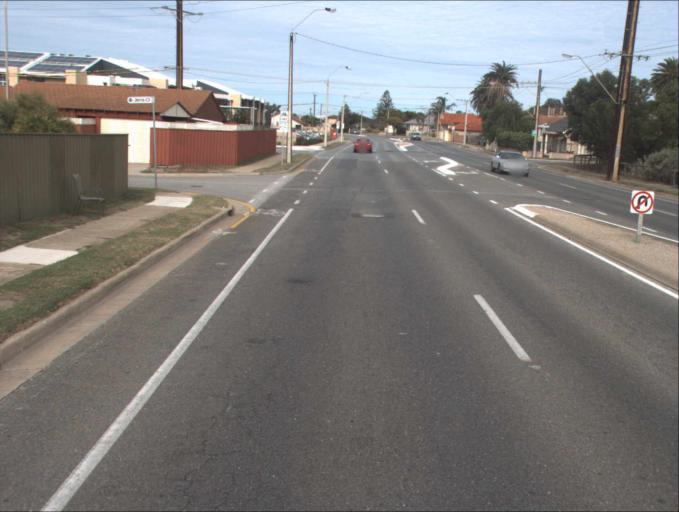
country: AU
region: South Australia
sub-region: Charles Sturt
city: West Lakes Shore
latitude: -34.8553
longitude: 138.4786
